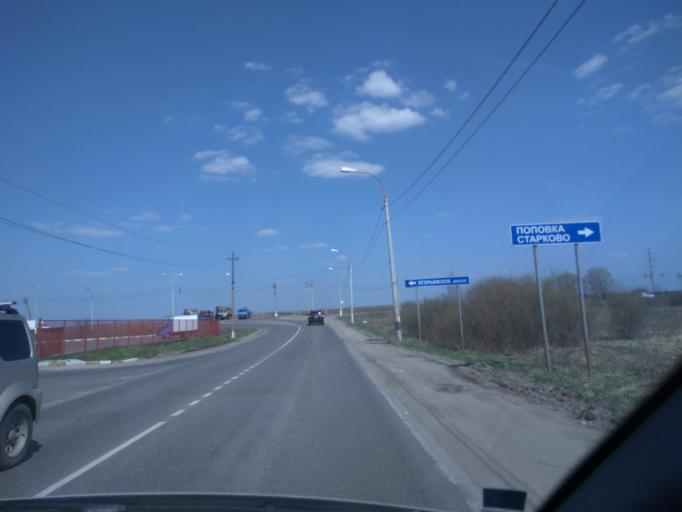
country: RU
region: Moskovskaya
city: Ramenskoye
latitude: 55.5785
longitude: 38.2712
